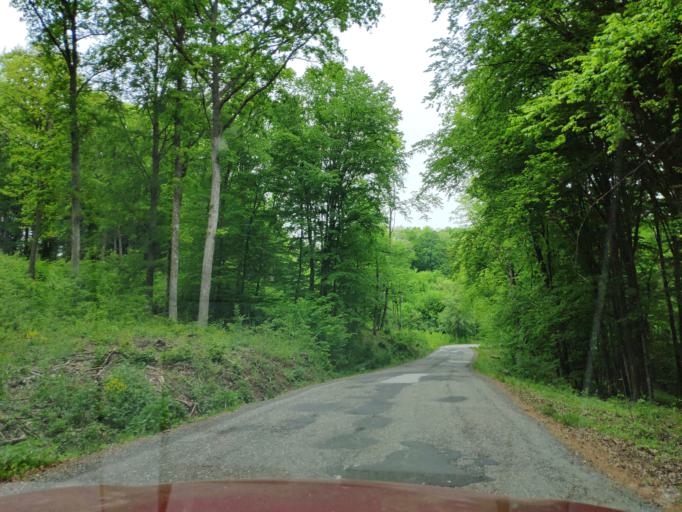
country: SK
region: Banskobystricky
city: Rimavska Sobota
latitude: 48.5108
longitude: 20.1016
